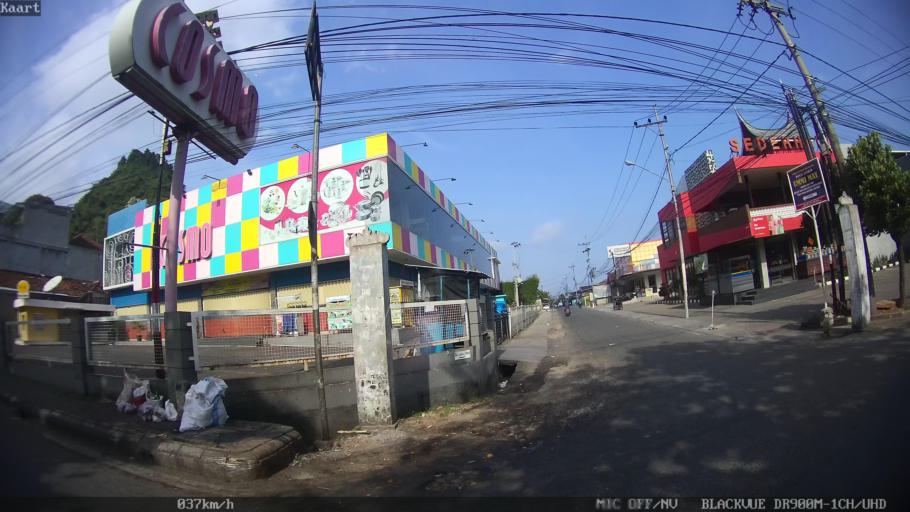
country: ID
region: Lampung
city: Kedaton
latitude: -5.3882
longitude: 105.2616
